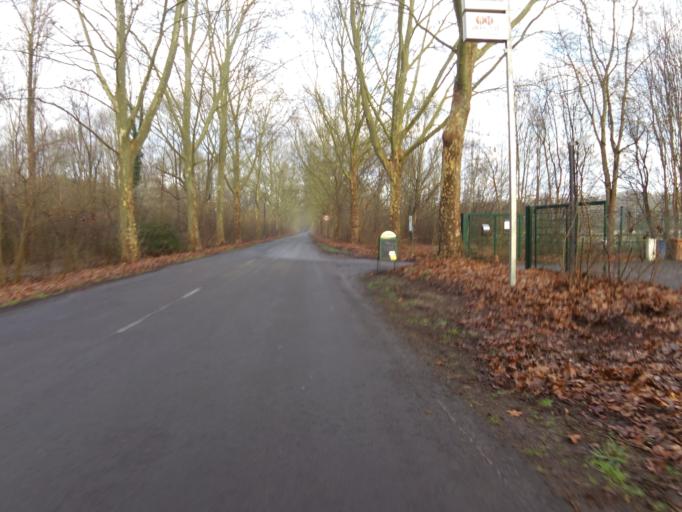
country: DE
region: Rheinland-Pfalz
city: Worms
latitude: 49.6160
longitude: 8.3820
